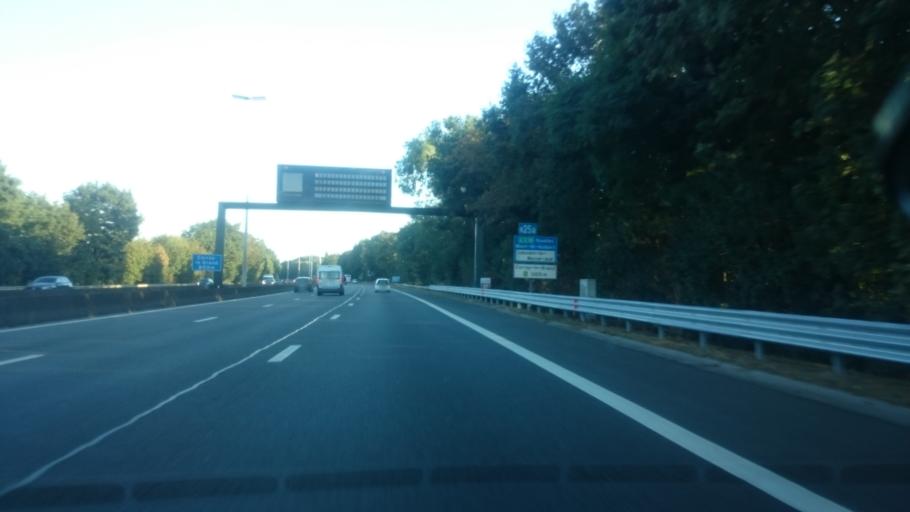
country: BE
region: Wallonia
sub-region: Province du Brabant Wallon
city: Louvain-la-Neuve
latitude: 50.6717
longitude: 4.6322
